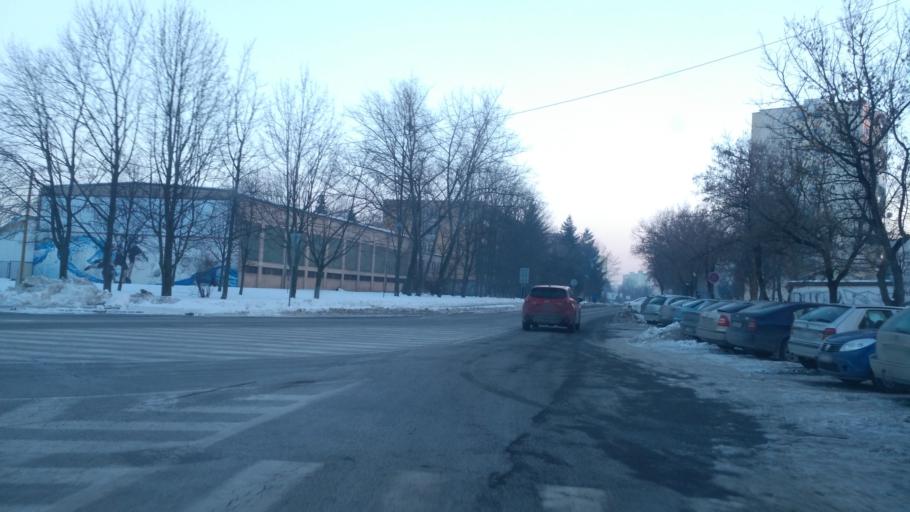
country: SK
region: Kosicky
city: Kosice
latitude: 48.7209
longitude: 21.2390
